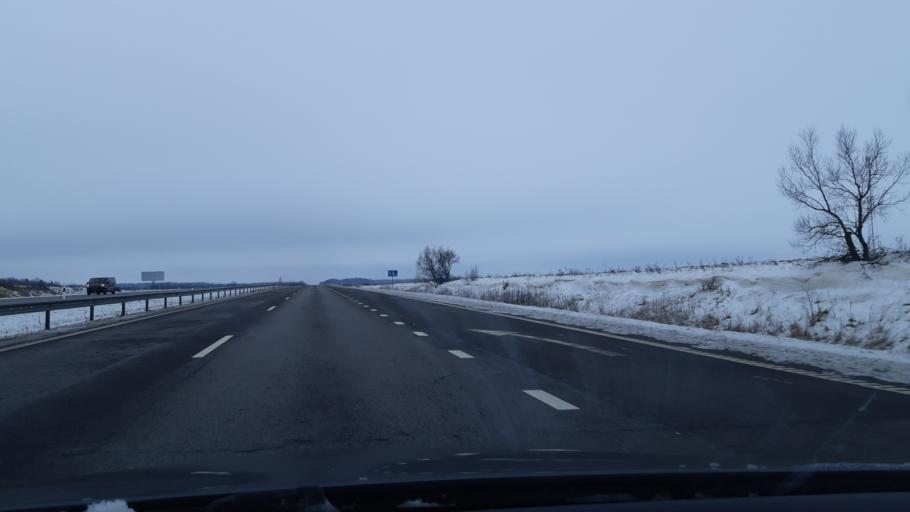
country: LT
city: Vilkija
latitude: 55.1124
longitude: 23.7707
